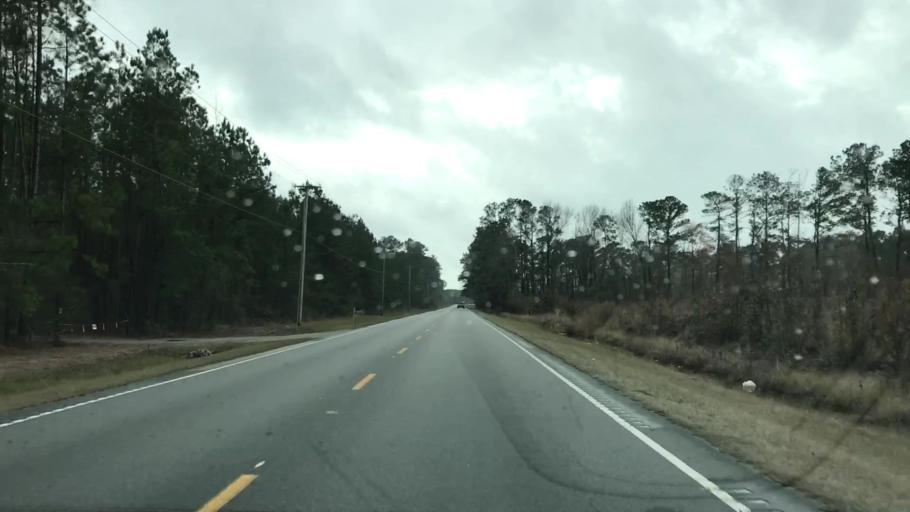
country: US
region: South Carolina
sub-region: Horry County
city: Socastee
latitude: 33.7320
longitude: -79.0831
